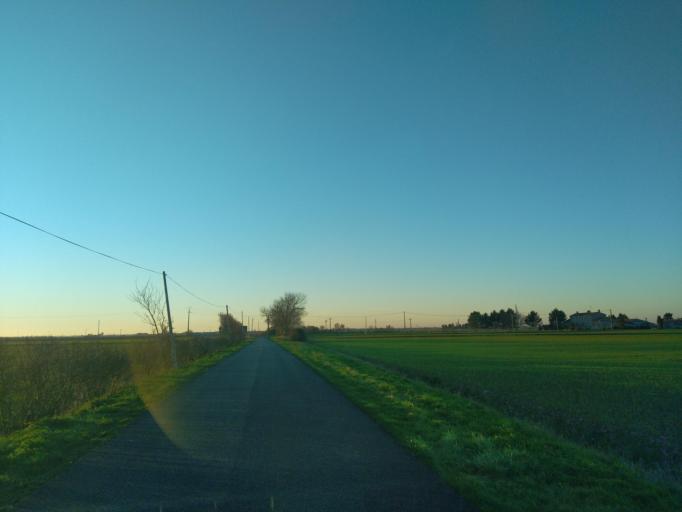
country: FR
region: Pays de la Loire
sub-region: Departement de la Vendee
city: Angles
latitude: 46.3786
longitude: -1.3108
